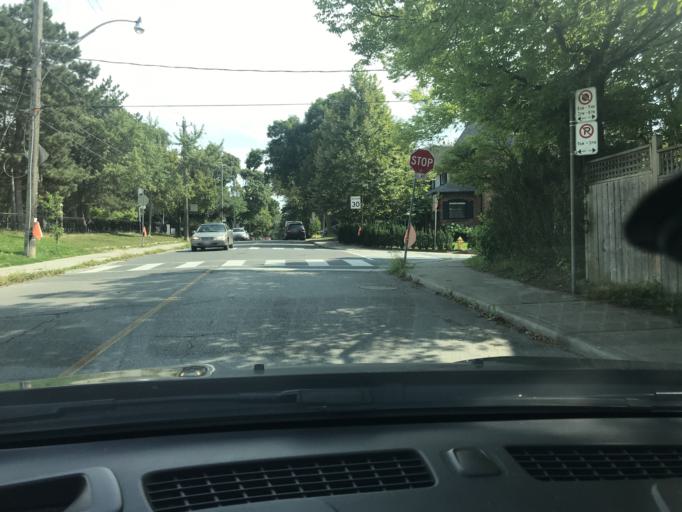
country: CA
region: Ontario
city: Toronto
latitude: 43.7191
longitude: -79.4100
